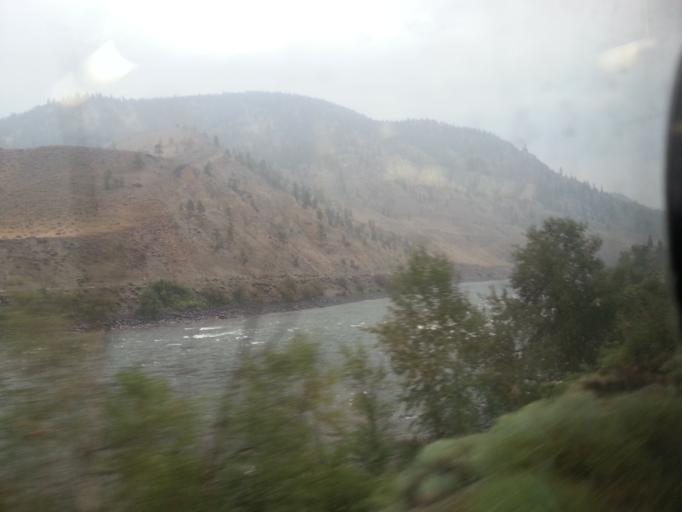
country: CA
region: British Columbia
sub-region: Thompson-Nicola Regional District
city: Ashcroft
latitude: 50.4657
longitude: -121.2980
